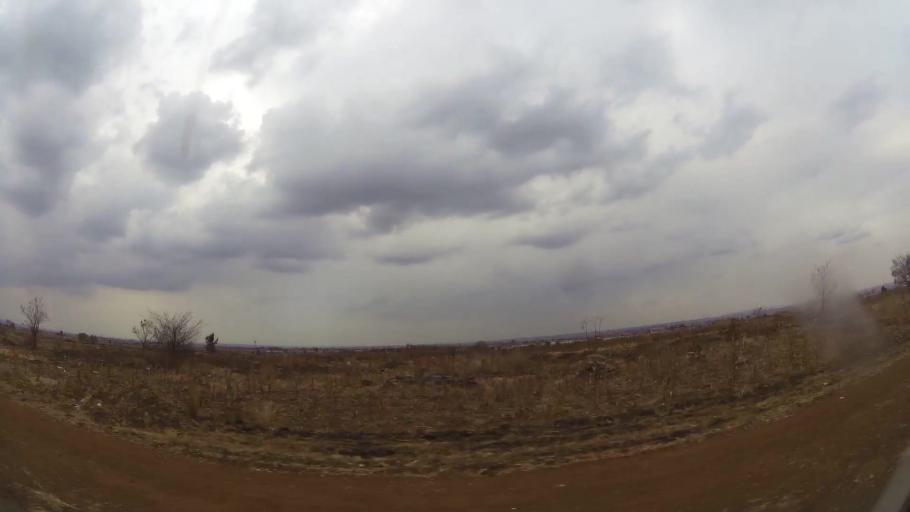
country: ZA
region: Gauteng
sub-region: Ekurhuleni Metropolitan Municipality
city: Germiston
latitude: -26.3830
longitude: 28.1444
